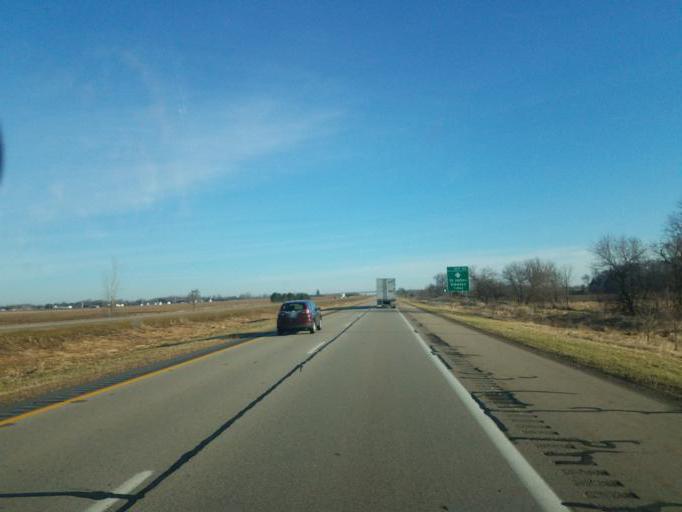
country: US
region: Michigan
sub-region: Clinton County
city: Saint Johns
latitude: 42.9761
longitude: -84.5185
